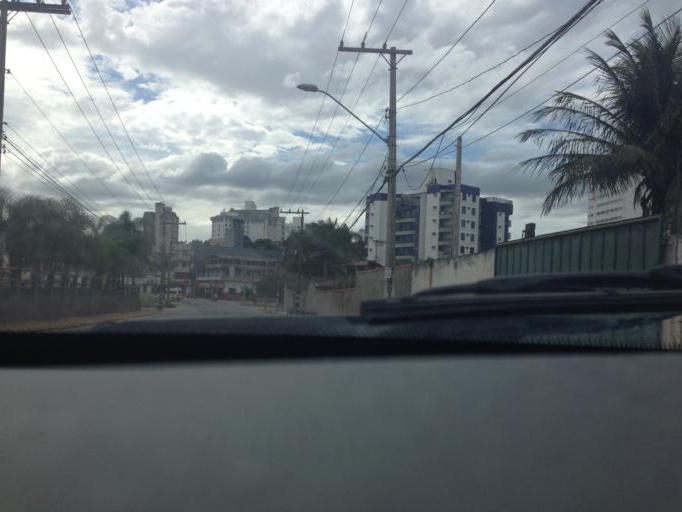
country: BR
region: Espirito Santo
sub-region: Guarapari
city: Guarapari
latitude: -20.6803
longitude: -40.5043
